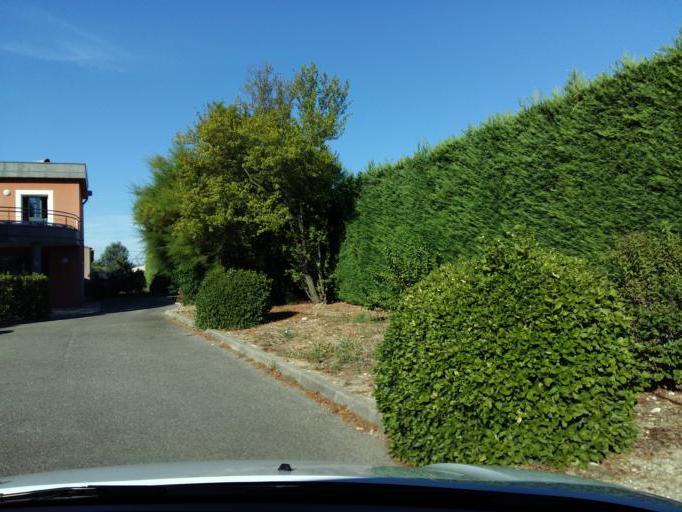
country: FR
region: Provence-Alpes-Cote d'Azur
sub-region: Departement du Vaucluse
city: Gargas
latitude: 43.8899
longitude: 5.3765
